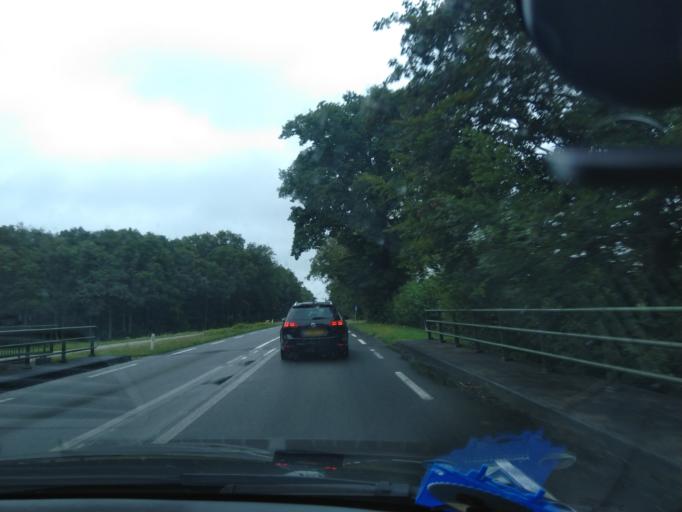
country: NL
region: Overijssel
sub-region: Gemeente Oldenzaal
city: Oldenzaal
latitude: 52.3659
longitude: 6.9945
